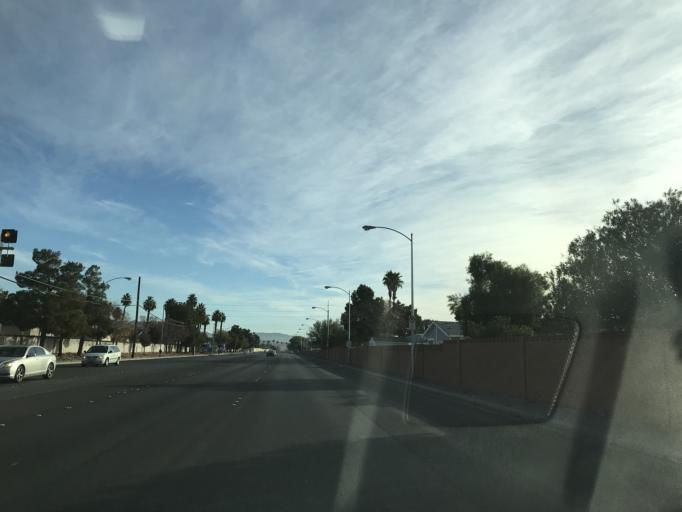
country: US
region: Nevada
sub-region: Clark County
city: Winchester
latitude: 36.1296
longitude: -115.0606
